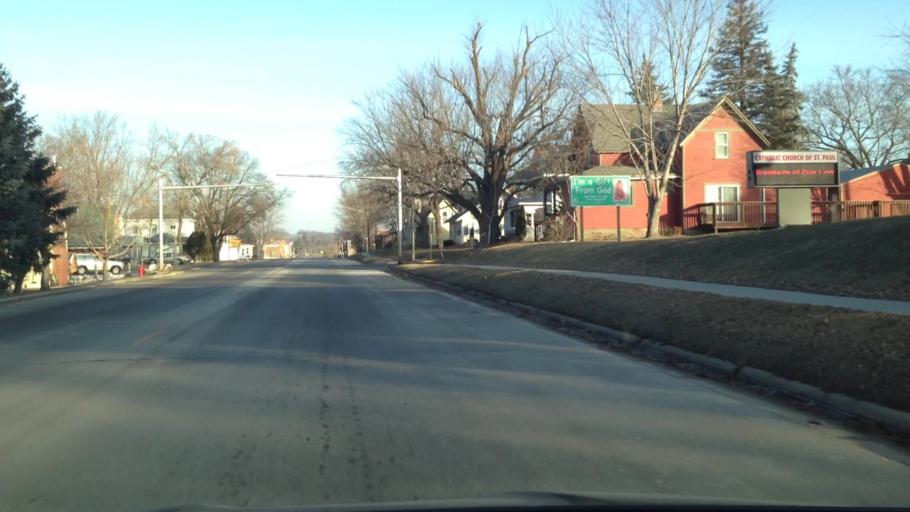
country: US
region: Minnesota
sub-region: Goodhue County
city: Zumbrota
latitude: 44.2901
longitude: -92.6691
